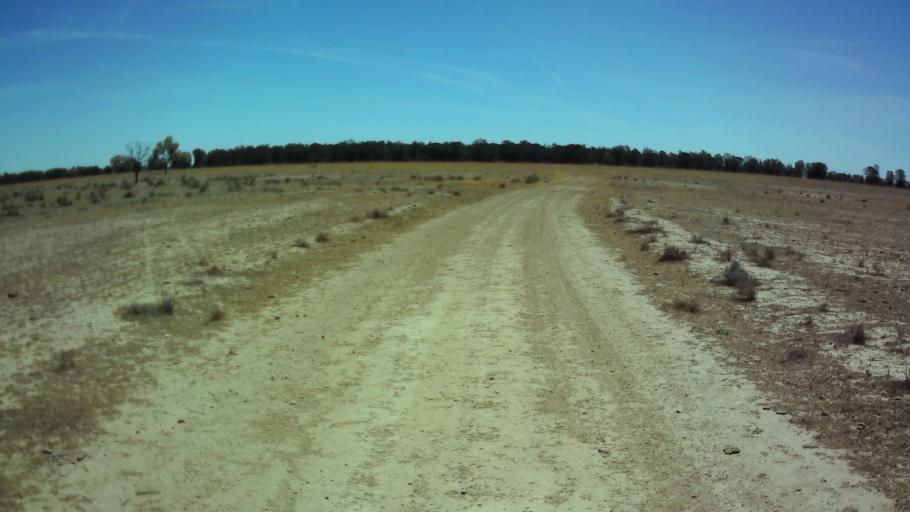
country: AU
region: New South Wales
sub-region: Bland
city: West Wyalong
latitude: -33.8386
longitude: 147.6315
